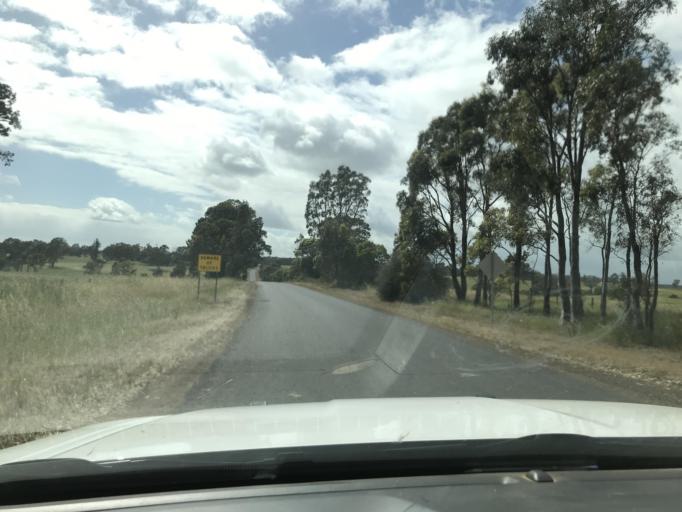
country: AU
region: South Australia
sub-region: Wattle Range
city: Penola
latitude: -37.1453
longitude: 141.3867
